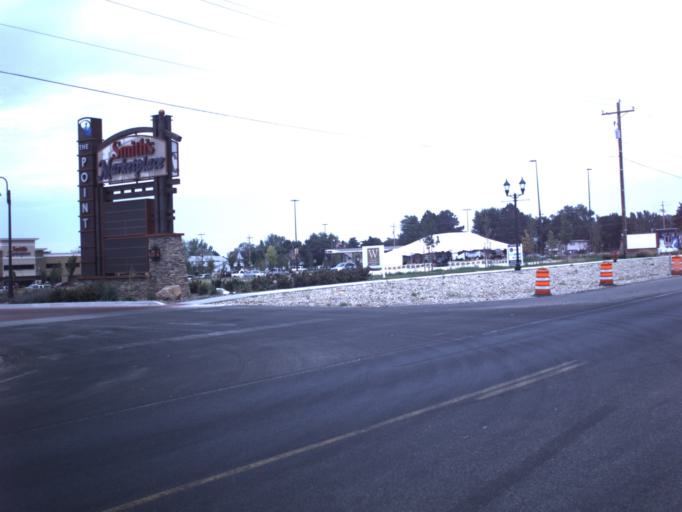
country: US
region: Utah
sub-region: Davis County
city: West Point
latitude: 41.1158
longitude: -112.0645
